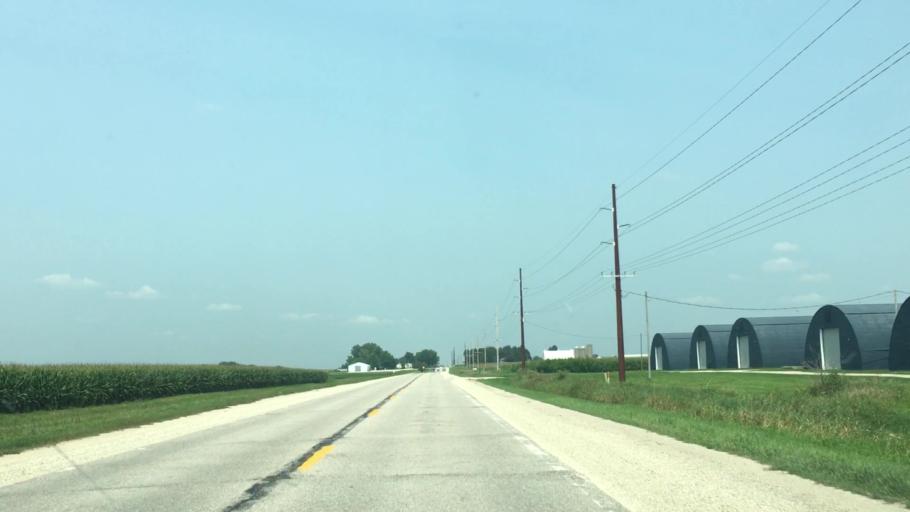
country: US
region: Iowa
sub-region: Buchanan County
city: Independence
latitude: 42.4129
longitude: -91.8899
